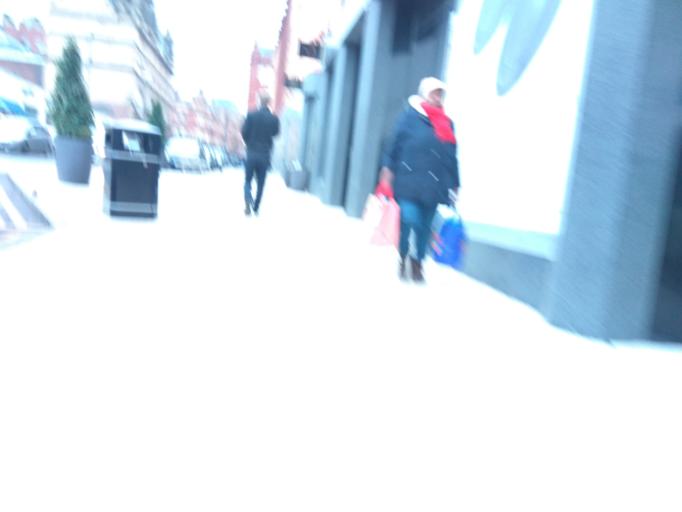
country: GB
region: England
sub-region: City and Borough of Leeds
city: Leeds
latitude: 53.7978
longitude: -1.5383
